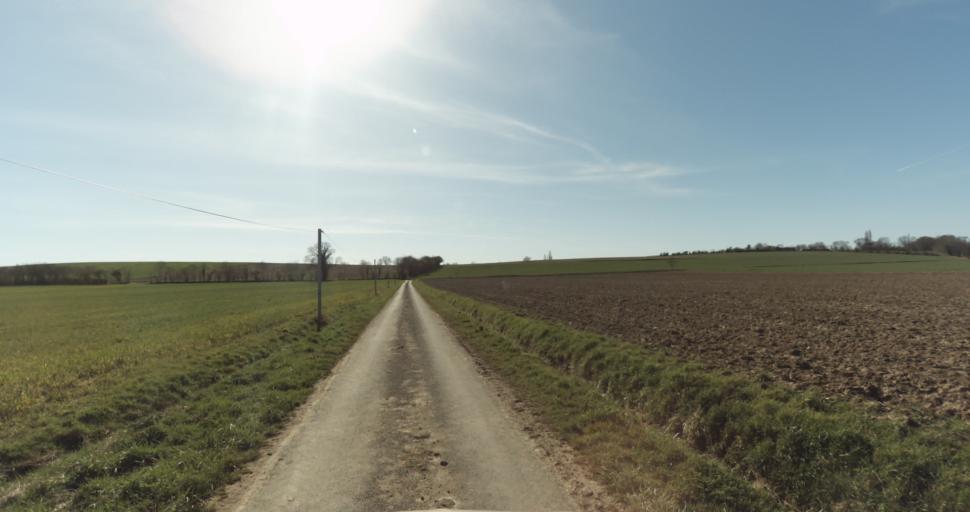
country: FR
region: Lower Normandy
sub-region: Departement du Calvados
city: Saint-Pierre-sur-Dives
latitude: 49.0234
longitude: 0.0160
